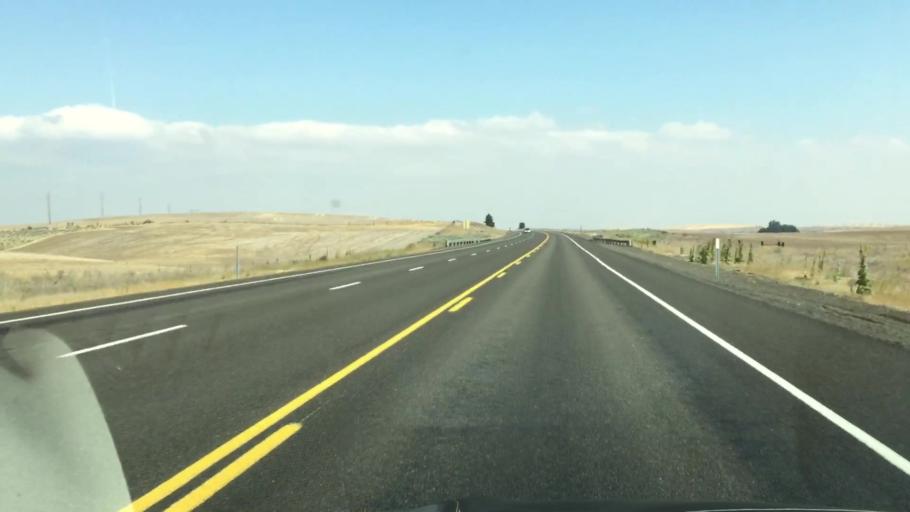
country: US
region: Oregon
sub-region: Wasco County
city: The Dalles
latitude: 45.4009
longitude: -121.1405
